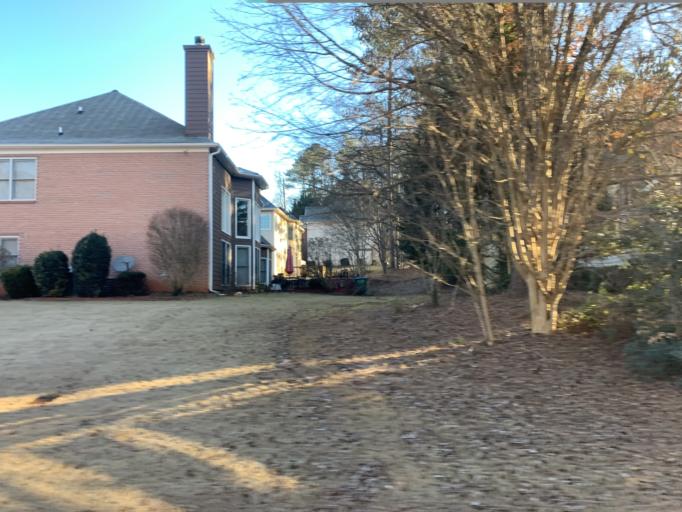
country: US
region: Georgia
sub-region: Gwinnett County
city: Mountain Park
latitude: 33.8655
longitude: -84.1103
